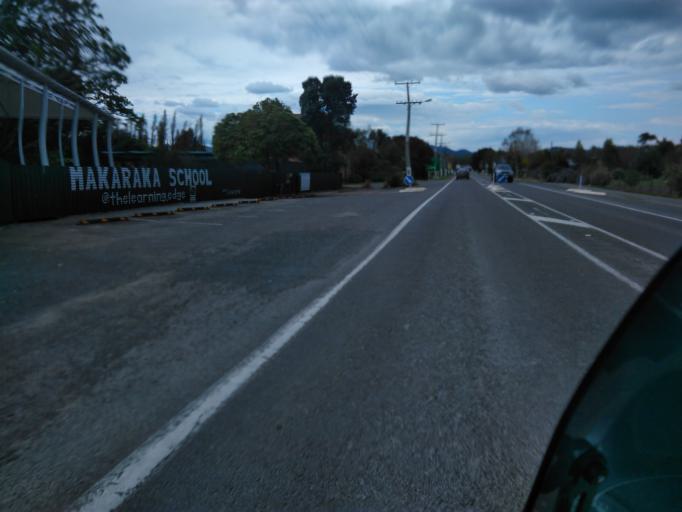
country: NZ
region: Gisborne
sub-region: Gisborne District
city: Gisborne
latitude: -38.6516
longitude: 177.9602
